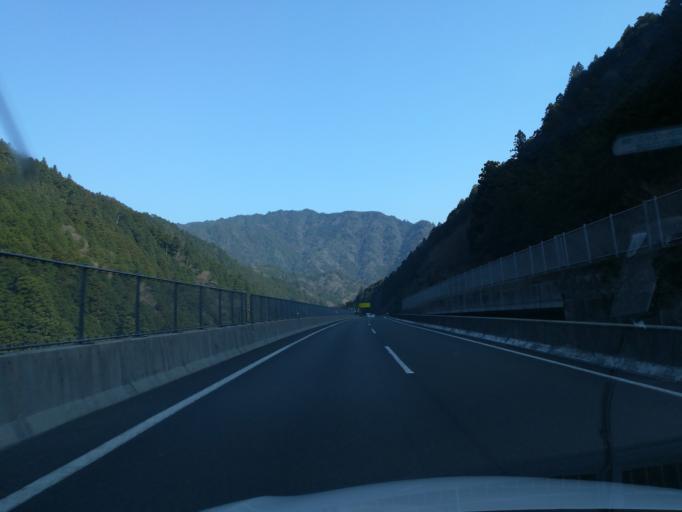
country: JP
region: Ehime
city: Kawanoecho
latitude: 33.9021
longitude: 133.6314
